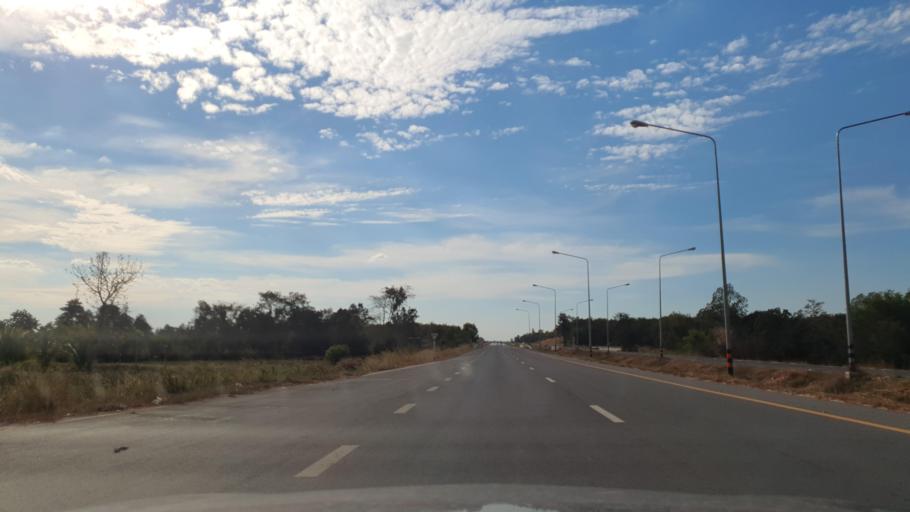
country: TH
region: Roi Et
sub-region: Amphoe Pho Chai
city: Pho Chai
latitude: 16.4139
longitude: 103.7906
